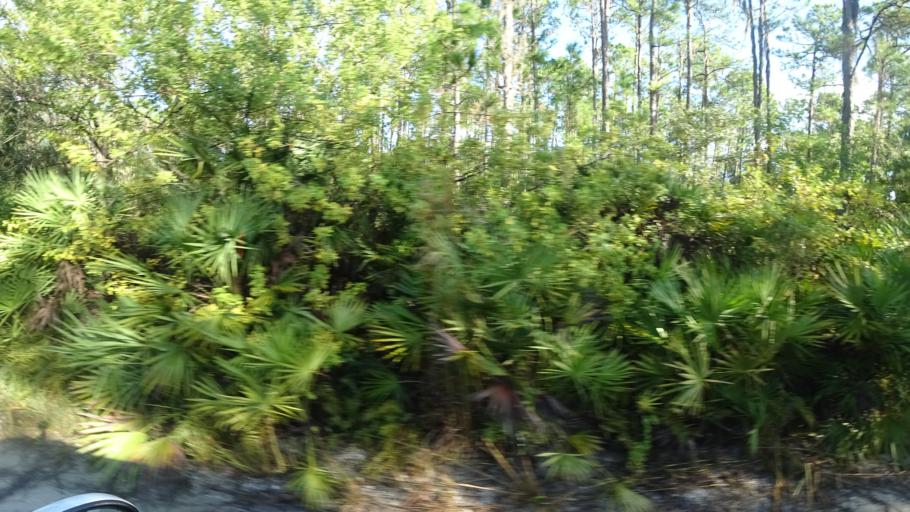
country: US
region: Florida
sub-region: Sarasota County
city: The Meadows
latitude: 27.4311
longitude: -82.3168
